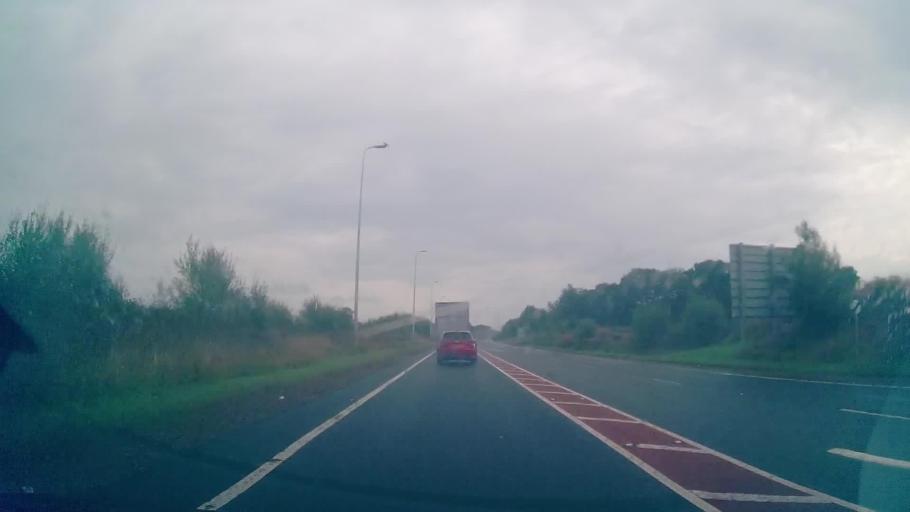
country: GB
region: Scotland
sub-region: Dumfries and Galloway
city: Lockerbie
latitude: 55.0313
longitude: -3.3997
